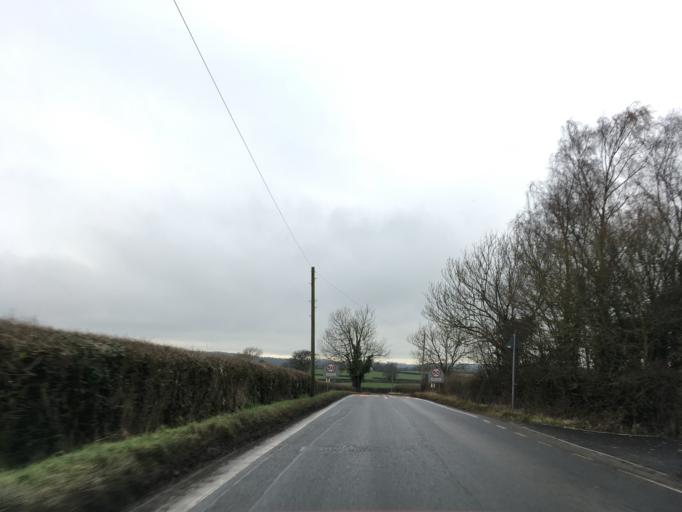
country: GB
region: England
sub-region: Gloucestershire
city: Wotton-under-Edge
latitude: 51.6279
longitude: -2.3729
